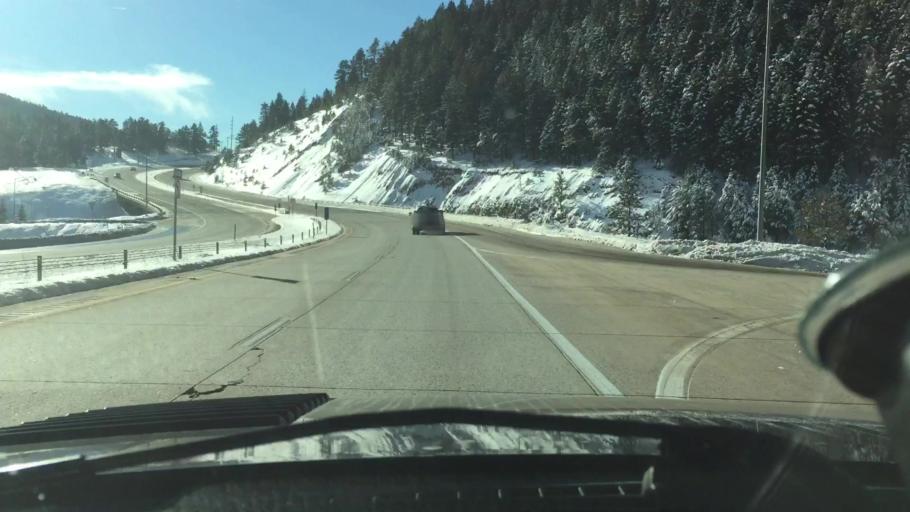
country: US
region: Colorado
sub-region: Jefferson County
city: Indian Hills
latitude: 39.5931
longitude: -105.2226
